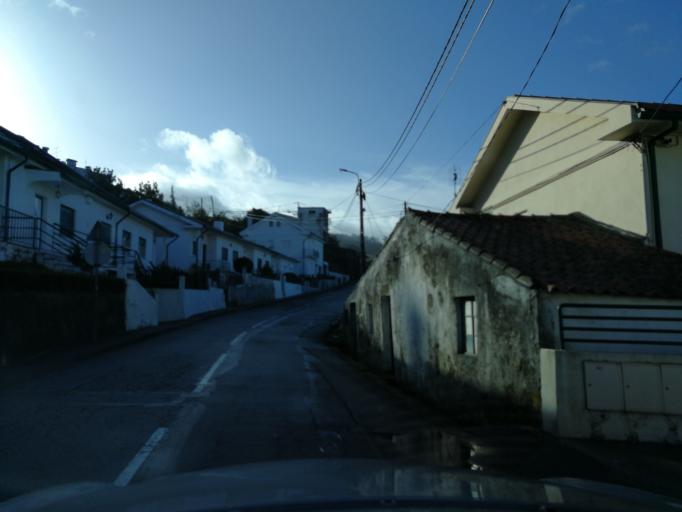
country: PT
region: Braga
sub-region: Braga
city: Braga
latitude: 41.5504
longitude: -8.3887
